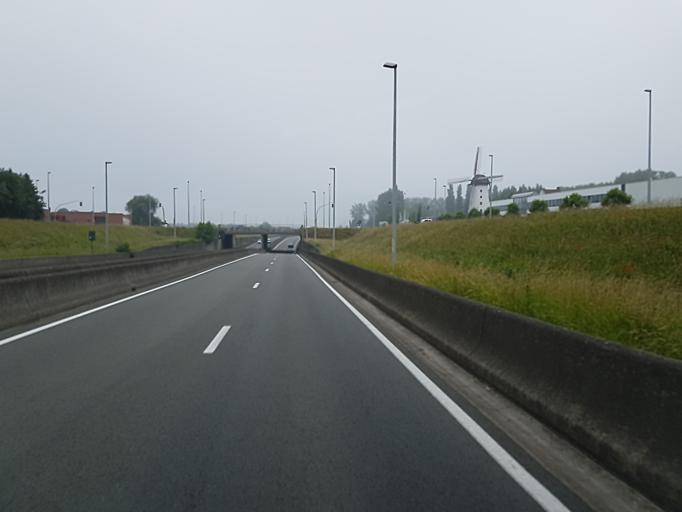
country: BE
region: Flanders
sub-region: Provincie West-Vlaanderen
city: Menen
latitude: 50.7974
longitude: 3.1365
